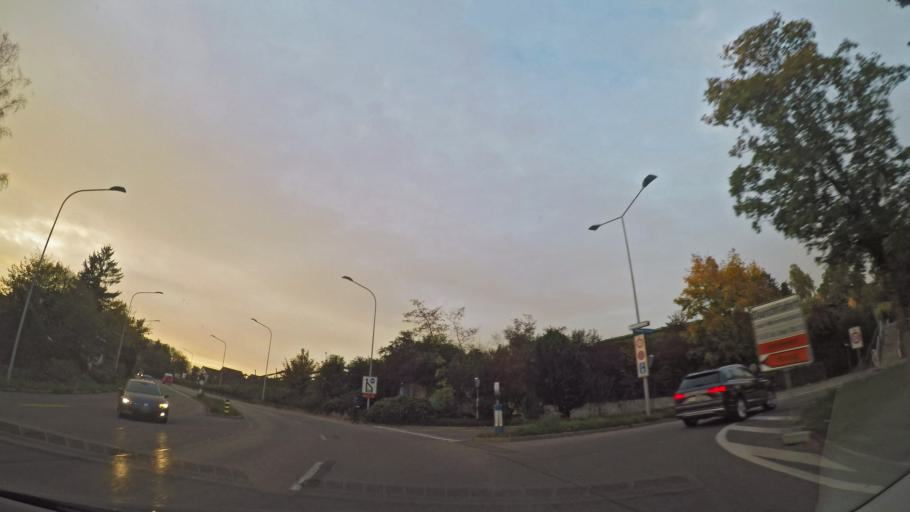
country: CH
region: Zurich
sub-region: Bezirk Zuerich
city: Zuerich (Kreis 10) / Ruetihof
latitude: 47.4067
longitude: 8.4812
